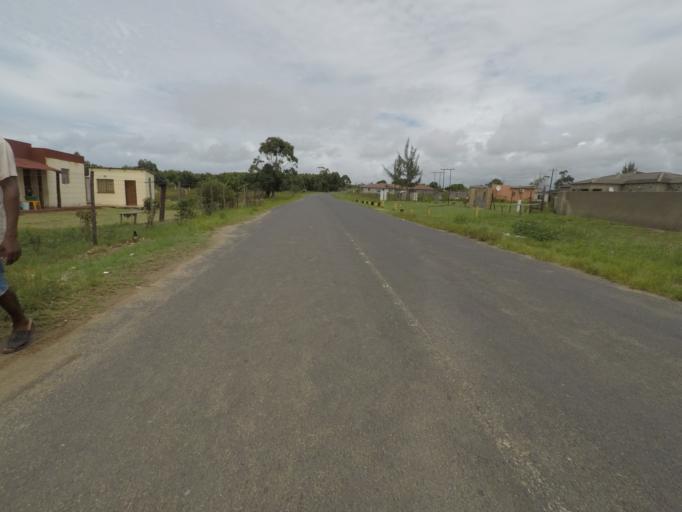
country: ZA
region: KwaZulu-Natal
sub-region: uThungulu District Municipality
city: eSikhawini
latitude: -28.9115
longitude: 31.8639
